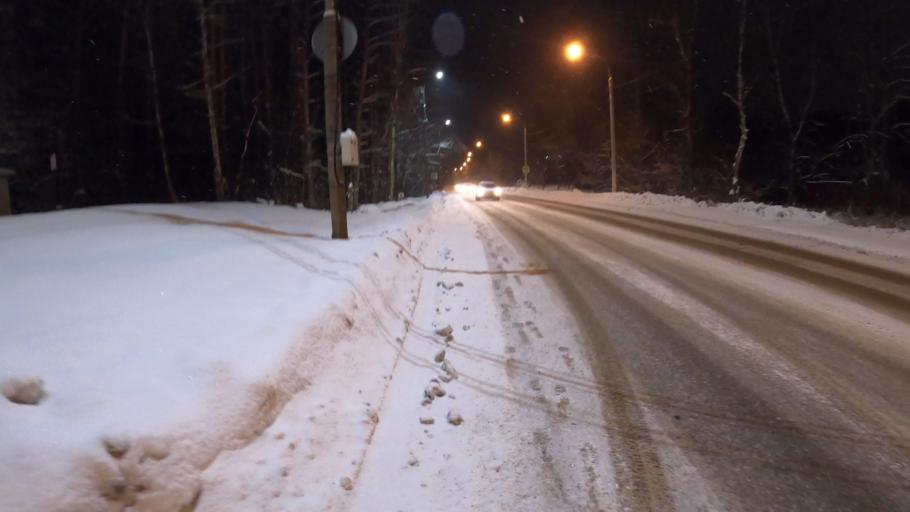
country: RU
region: Moskovskaya
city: Opalikha
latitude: 55.8402
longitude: 37.2212
